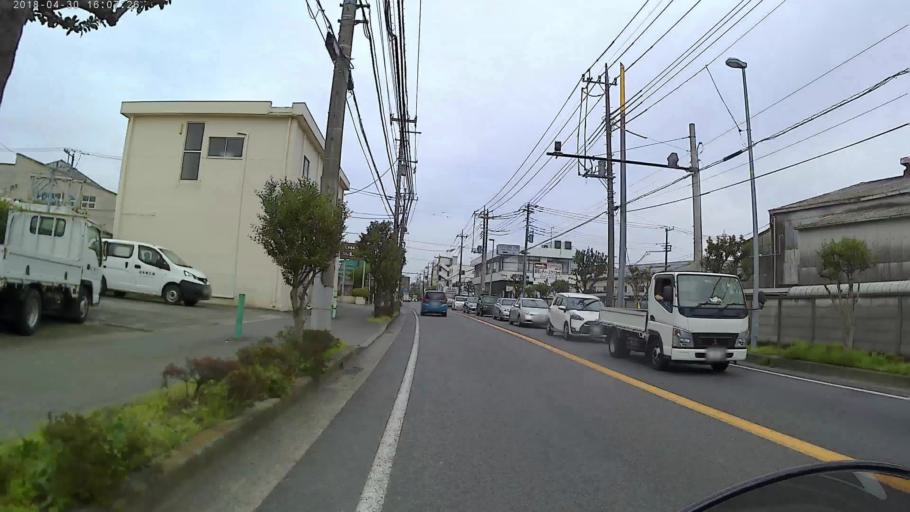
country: JP
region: Kanagawa
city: Minami-rinkan
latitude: 35.5011
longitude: 139.4332
